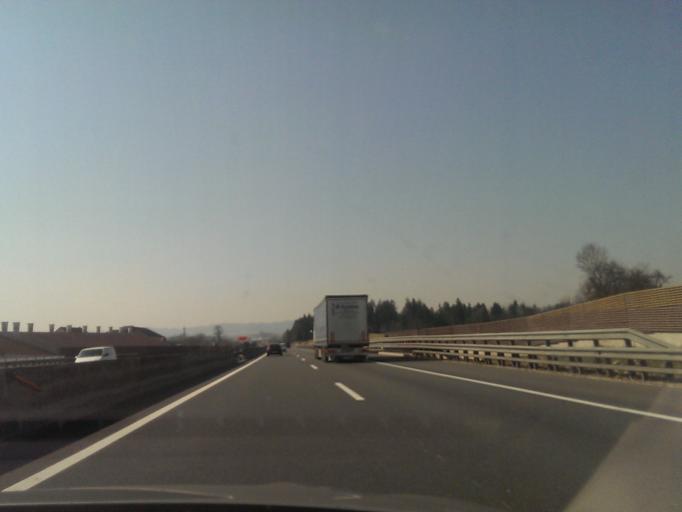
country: AT
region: Upper Austria
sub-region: Politischer Bezirk Vocklabruck
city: Niederthalheim
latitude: 48.1773
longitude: 13.7318
